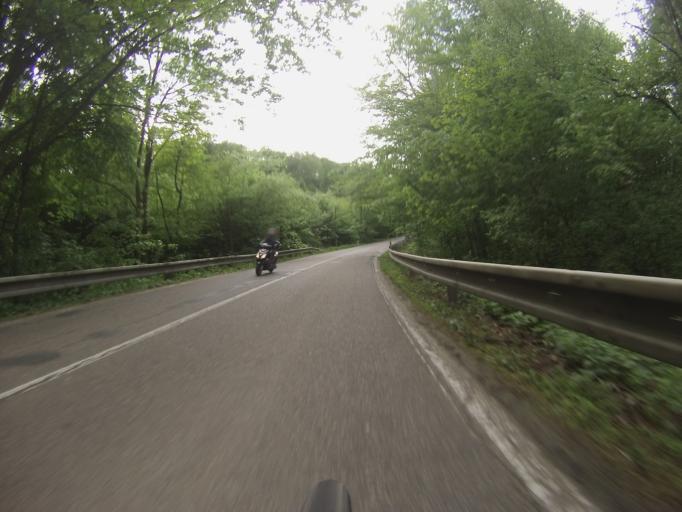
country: CZ
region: South Moravian
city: Veverska Bityska
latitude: 49.2520
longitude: 16.4815
